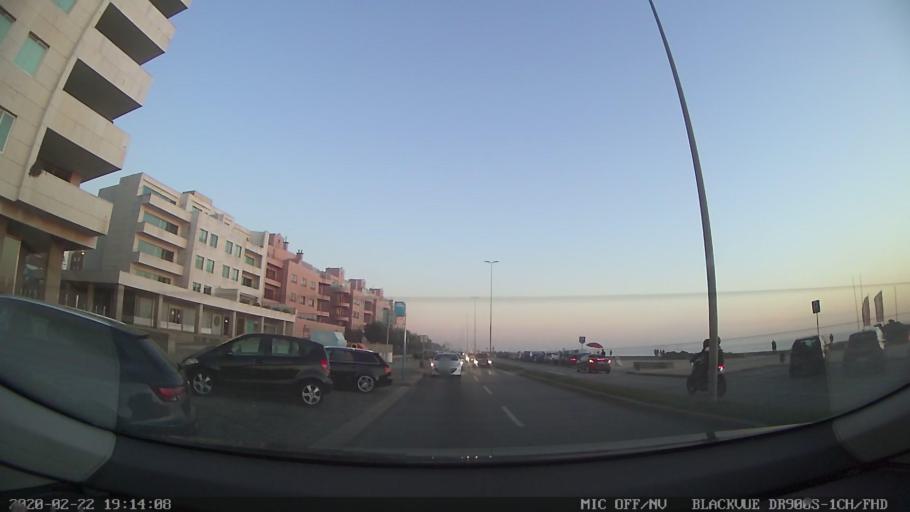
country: PT
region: Porto
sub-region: Matosinhos
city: Leca da Palmeira
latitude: 41.1972
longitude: -8.7095
